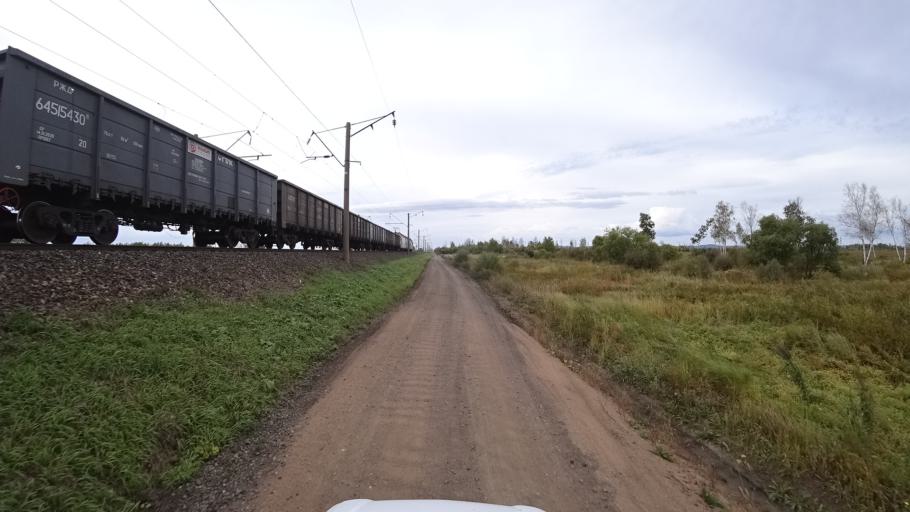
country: RU
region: Amur
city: Arkhara
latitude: 49.3584
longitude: 130.1517
